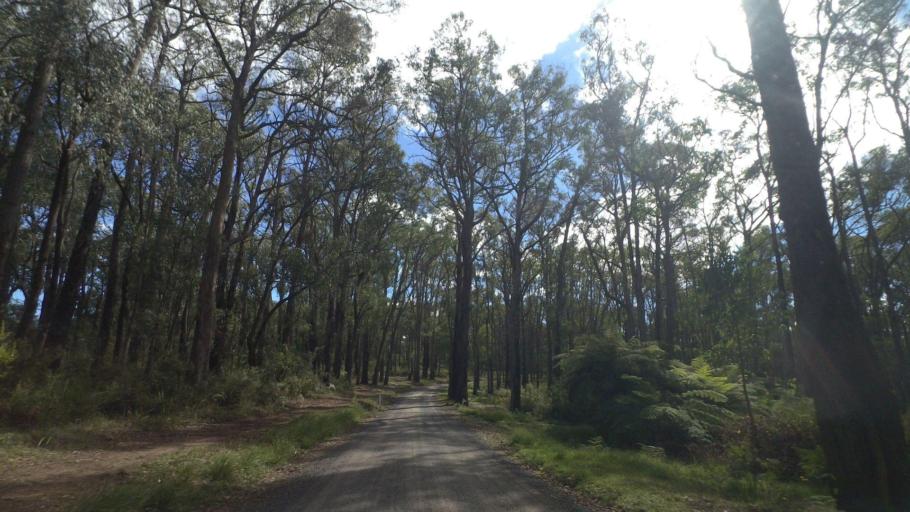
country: AU
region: Victoria
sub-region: Cardinia
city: Gembrook
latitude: -37.9065
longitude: 145.5918
